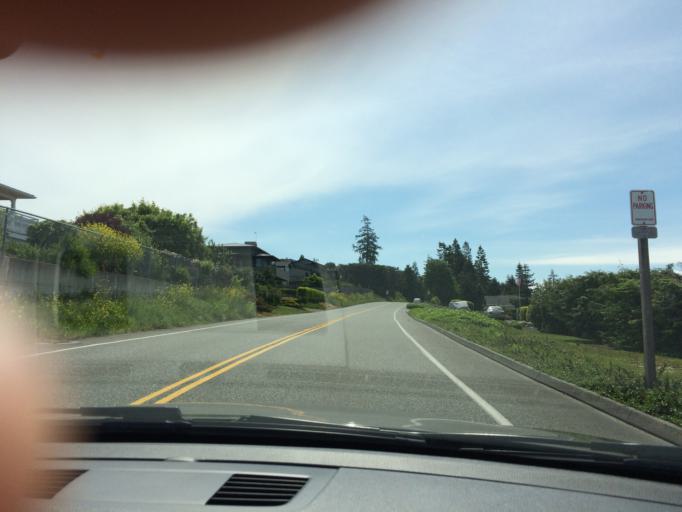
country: US
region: Washington
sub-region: Skagit County
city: Anacortes
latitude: 48.4972
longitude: -122.6729
